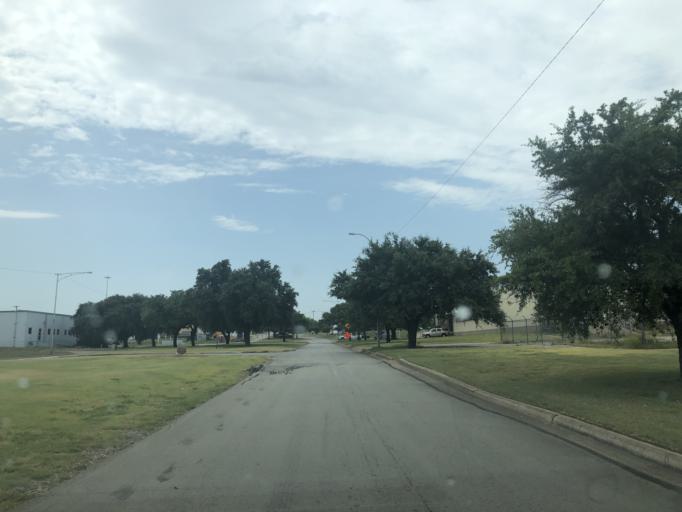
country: US
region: Texas
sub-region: Dallas County
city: Grand Prairie
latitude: 32.7636
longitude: -97.0459
